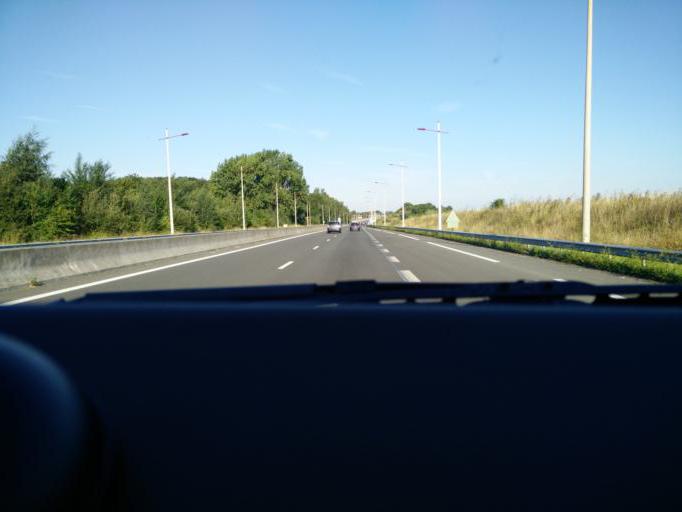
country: FR
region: Nord-Pas-de-Calais
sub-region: Departement du Pas-de-Calais
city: Bouvigny-Boyeffles
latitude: 50.4364
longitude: 2.6671
